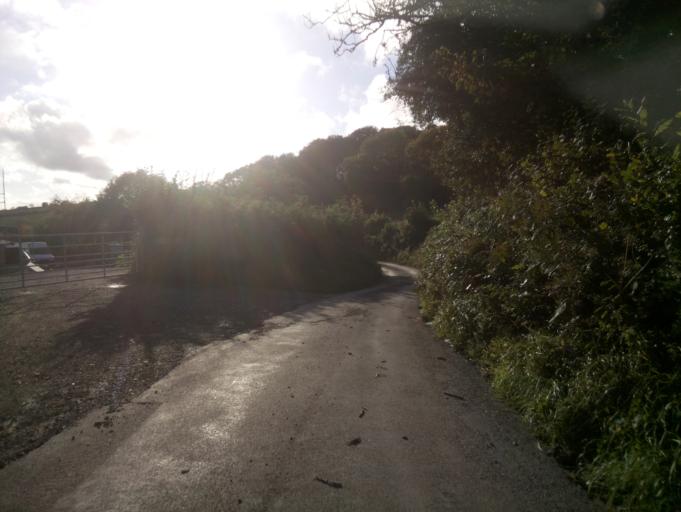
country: GB
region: England
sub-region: Devon
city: Dartmouth
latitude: 50.3457
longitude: -3.6653
